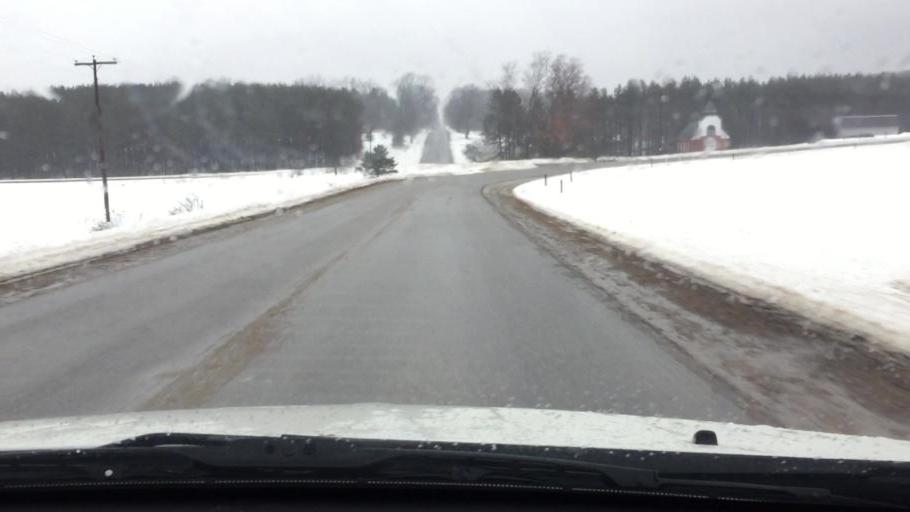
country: US
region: Michigan
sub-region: Charlevoix County
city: East Jordan
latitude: 45.1043
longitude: -85.1600
